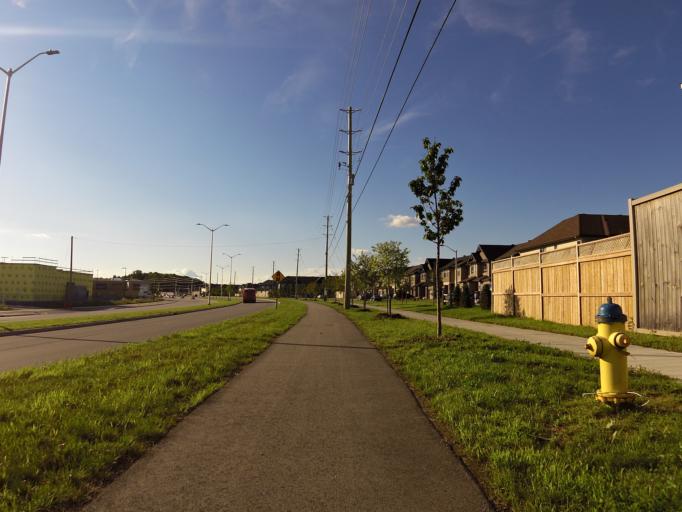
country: CA
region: Ontario
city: Bells Corners
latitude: 45.2694
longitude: -75.7802
